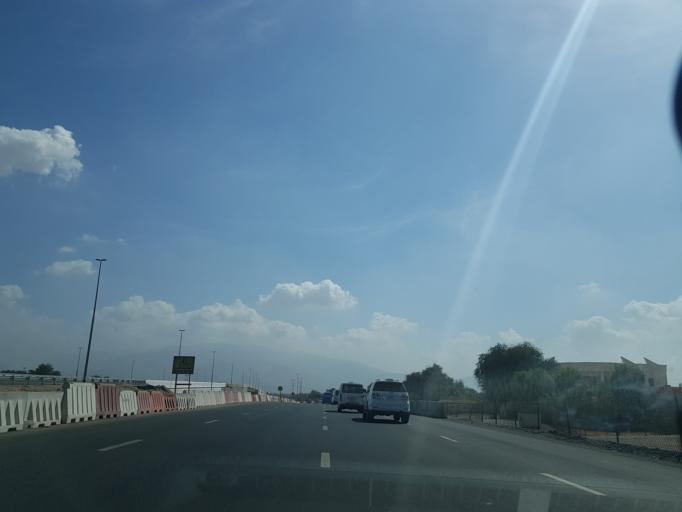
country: AE
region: Ra's al Khaymah
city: Ras al-Khaimah
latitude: 25.7008
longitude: 55.9631
